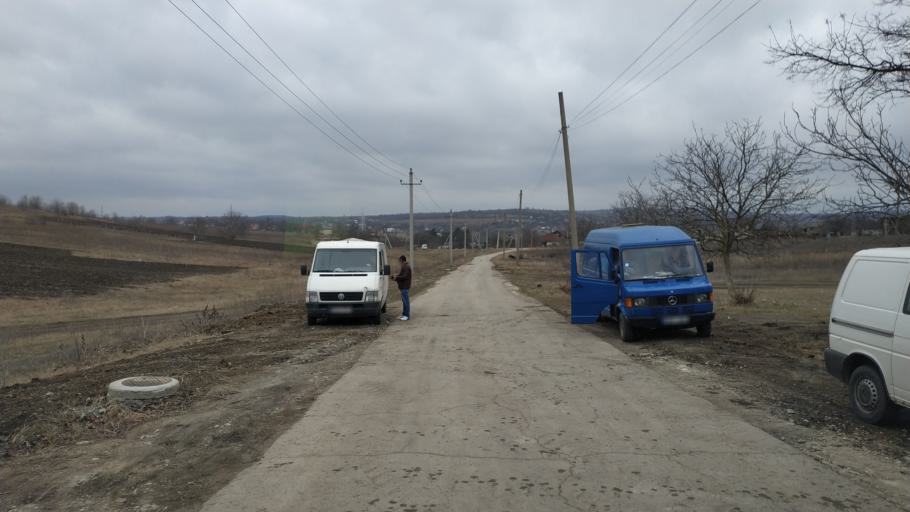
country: MD
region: Laloveni
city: Ialoveni
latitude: 46.9433
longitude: 28.7938
